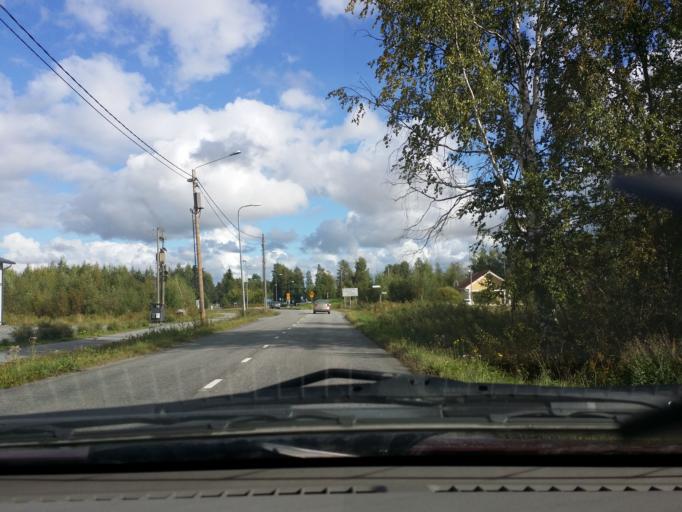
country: FI
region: Satakunta
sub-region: Pori
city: Pori
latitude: 61.4934
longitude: 21.8375
